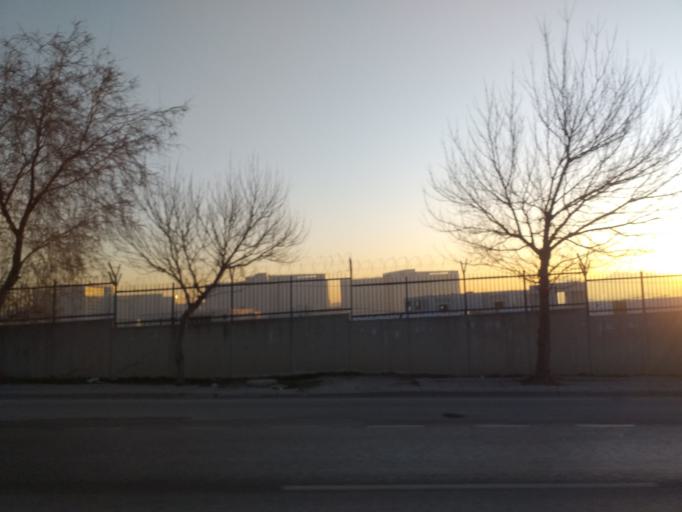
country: TR
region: Ankara
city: Ankara
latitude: 39.9605
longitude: 32.8225
